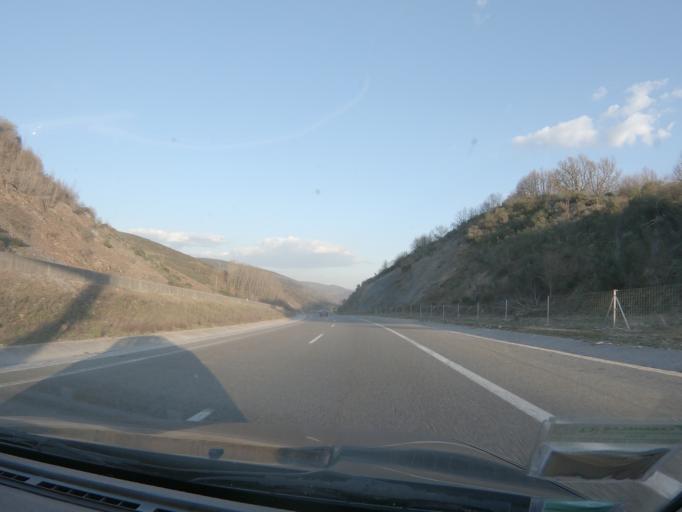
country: ES
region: Castille and Leon
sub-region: Provincia de Leon
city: Vega de Valcarce
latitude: 42.6699
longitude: -6.9543
